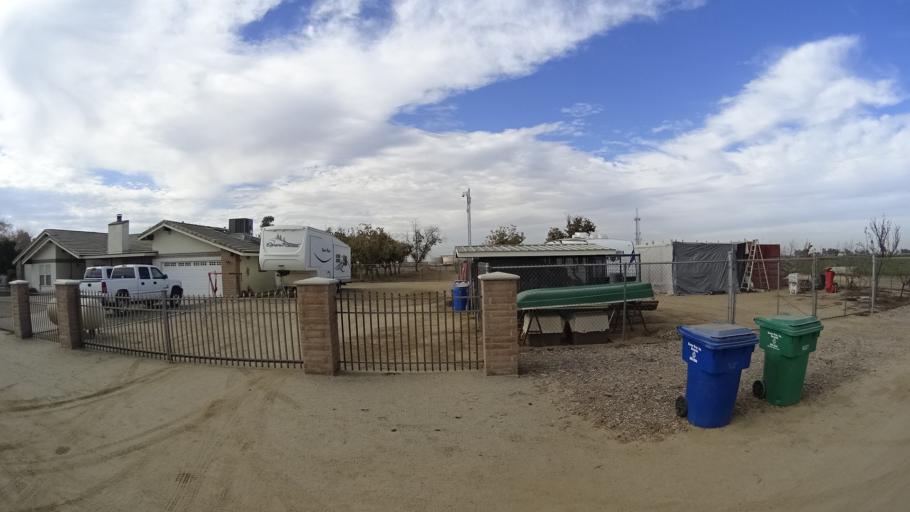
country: US
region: California
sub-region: Kern County
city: Rosedale
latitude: 35.4304
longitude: -119.1388
